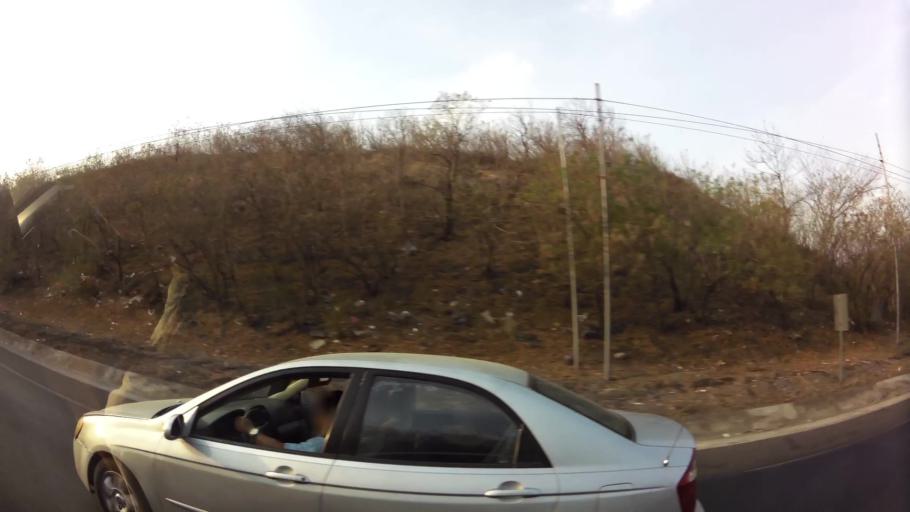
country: NI
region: Managua
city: Ciudad Sandino
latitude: 12.1338
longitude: -86.3235
